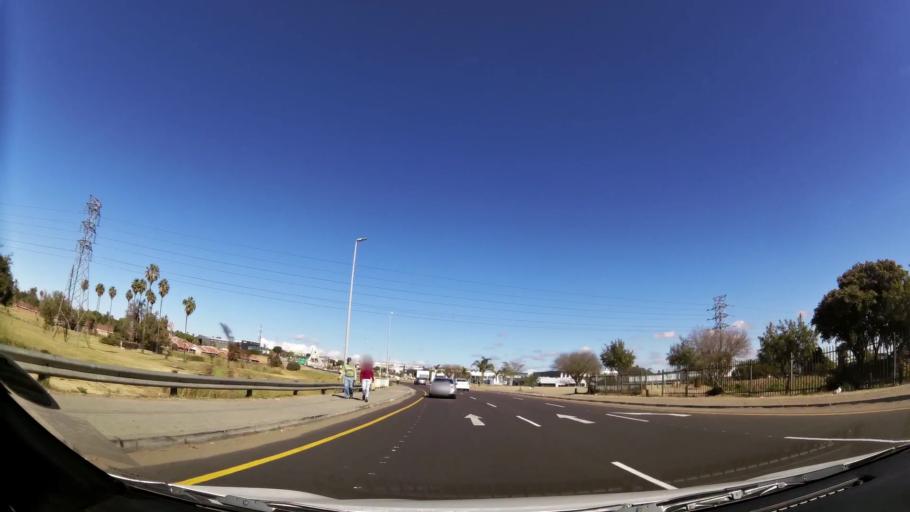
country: ZA
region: Limpopo
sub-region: Capricorn District Municipality
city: Polokwane
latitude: -23.9129
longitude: 29.4463
